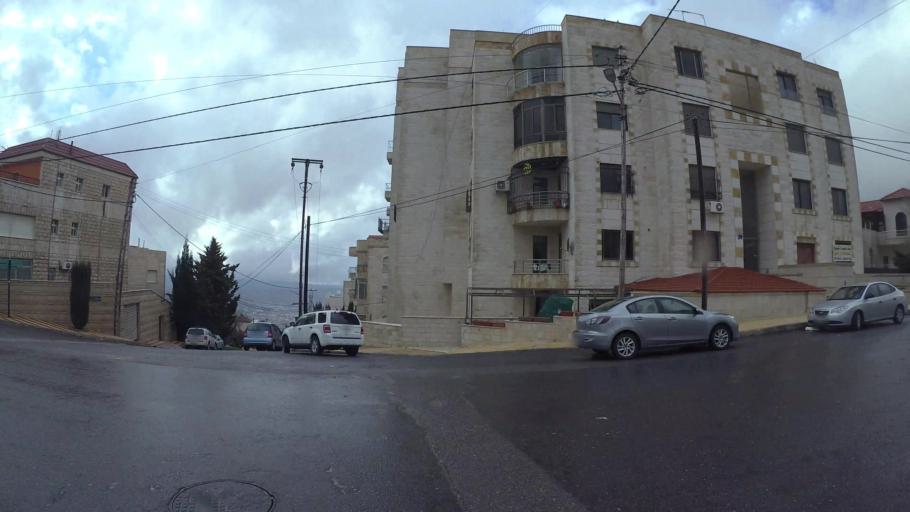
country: JO
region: Amman
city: Al Jubayhah
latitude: 32.0344
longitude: 35.8569
